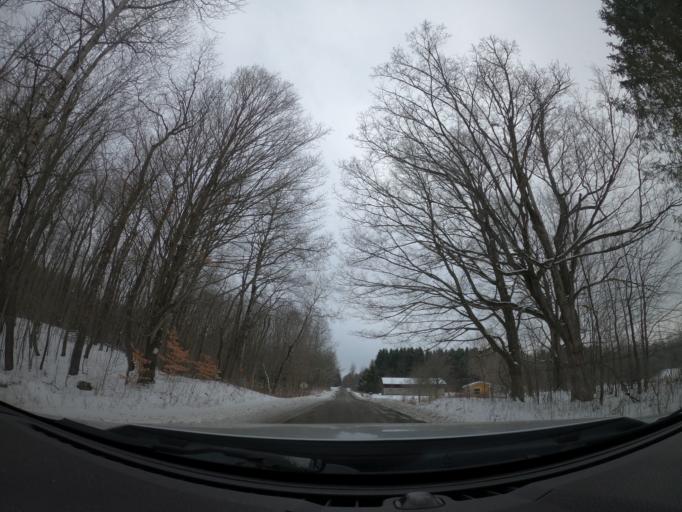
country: US
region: New York
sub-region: Cayuga County
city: Moravia
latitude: 42.7341
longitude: -76.2940
